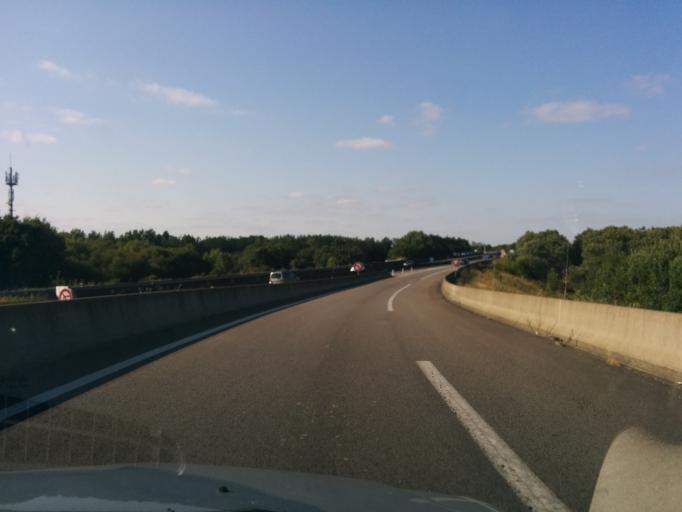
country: FR
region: Pays de la Loire
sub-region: Departement de la Loire-Atlantique
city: Sainte-Luce-sur-Loire
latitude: 47.2384
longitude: -1.4782
